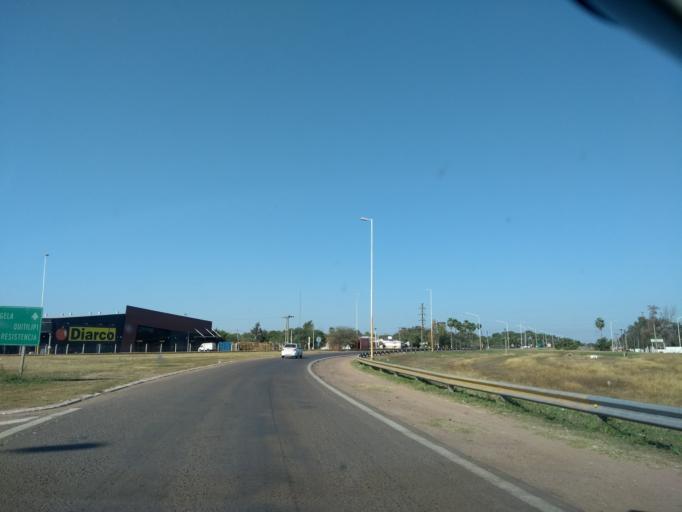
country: AR
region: Chaco
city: Presidencia Roque Saenz Pena
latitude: -26.8130
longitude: -60.4190
